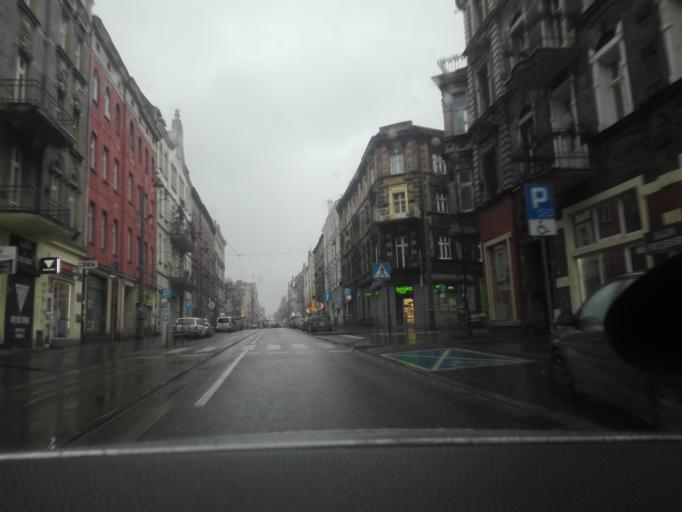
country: PL
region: Silesian Voivodeship
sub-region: Katowice
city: Katowice
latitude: 50.2559
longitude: 19.0187
